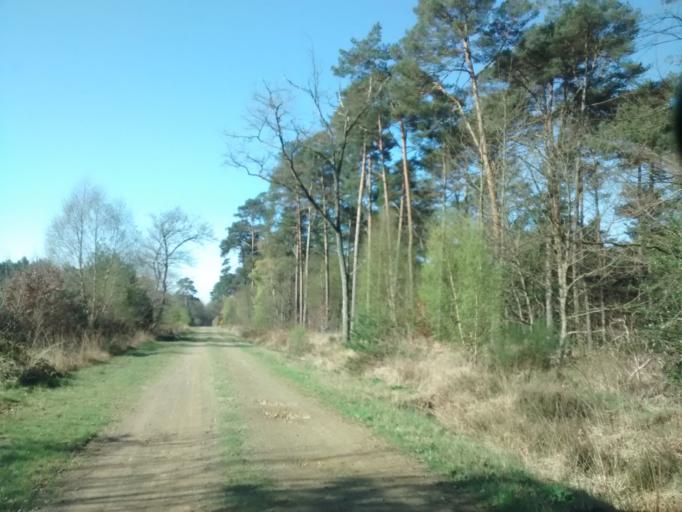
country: FR
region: Brittany
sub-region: Departement d'Ille-et-Vilaine
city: Liffre
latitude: 48.2159
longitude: -1.5345
